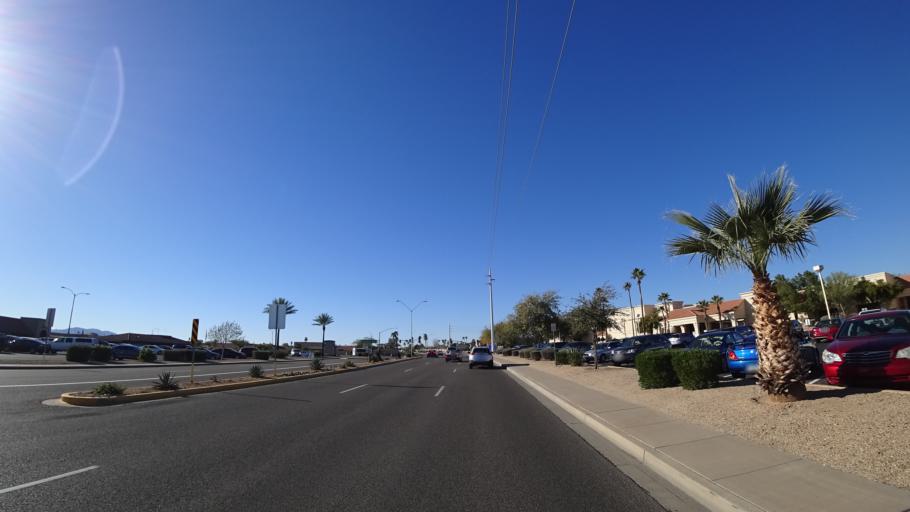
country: US
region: Arizona
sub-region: Maricopa County
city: Sun City West
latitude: 33.6701
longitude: -112.3702
